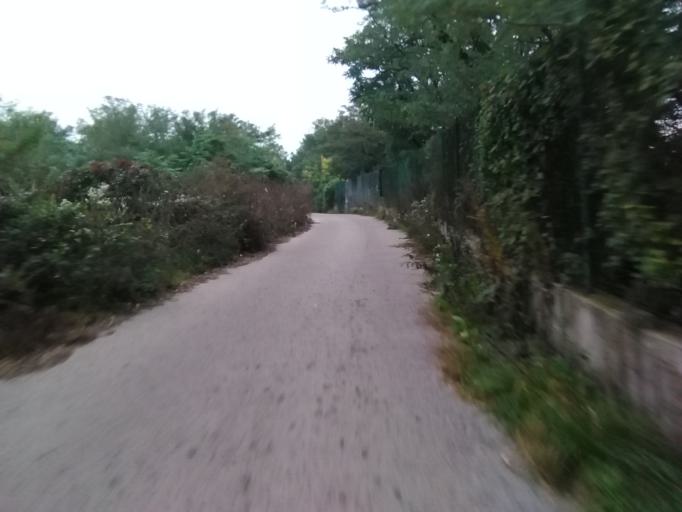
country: SK
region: Bratislavsky
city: Bratislava
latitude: 48.1790
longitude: 17.1216
